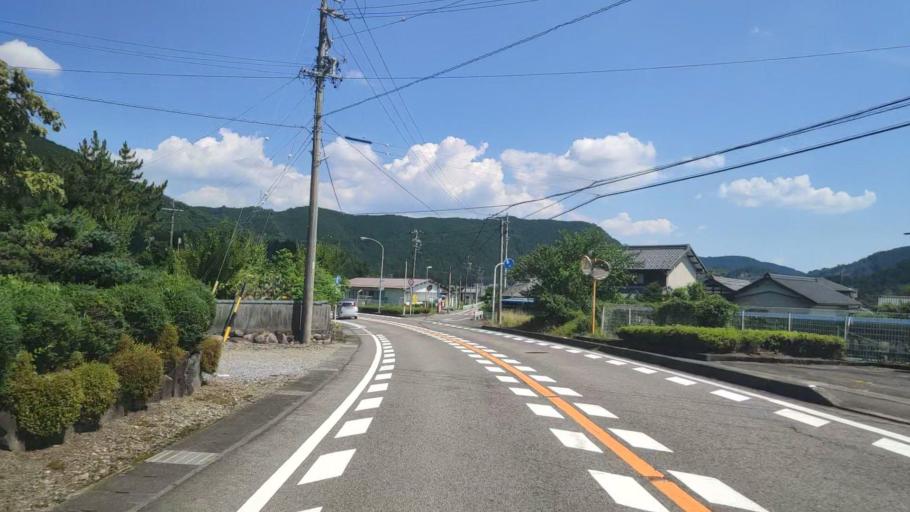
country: JP
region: Gifu
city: Godo
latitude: 35.5402
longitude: 136.6447
